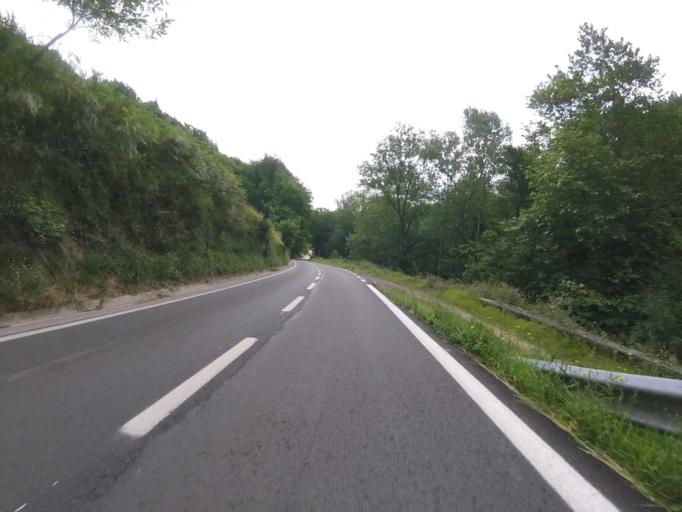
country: ES
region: Navarre
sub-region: Provincia de Navarra
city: Zubieta
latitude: 43.1261
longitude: -1.7450
